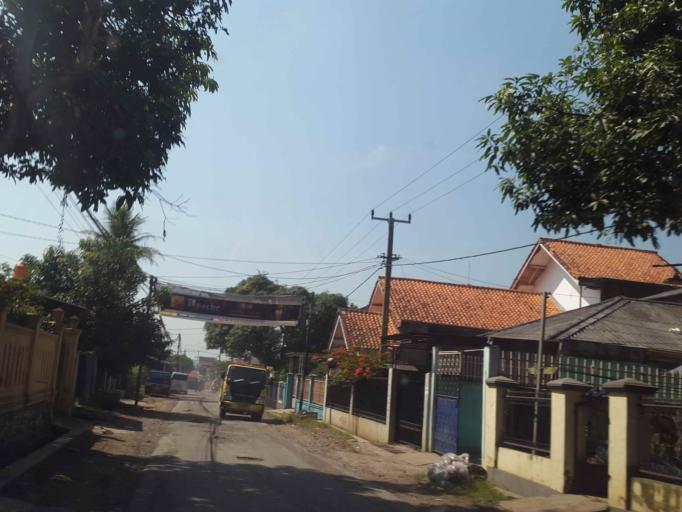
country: ID
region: West Java
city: Ciranjang-hilir
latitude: -6.8453
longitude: 107.1185
